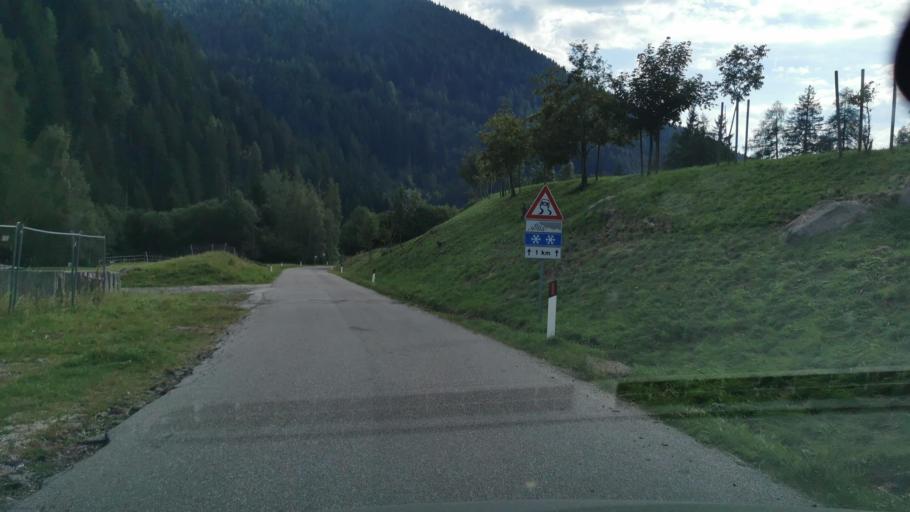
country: IT
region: Trentino-Alto Adige
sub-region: Provincia di Trento
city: Palu del Fersina
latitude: 46.1287
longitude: 11.3542
